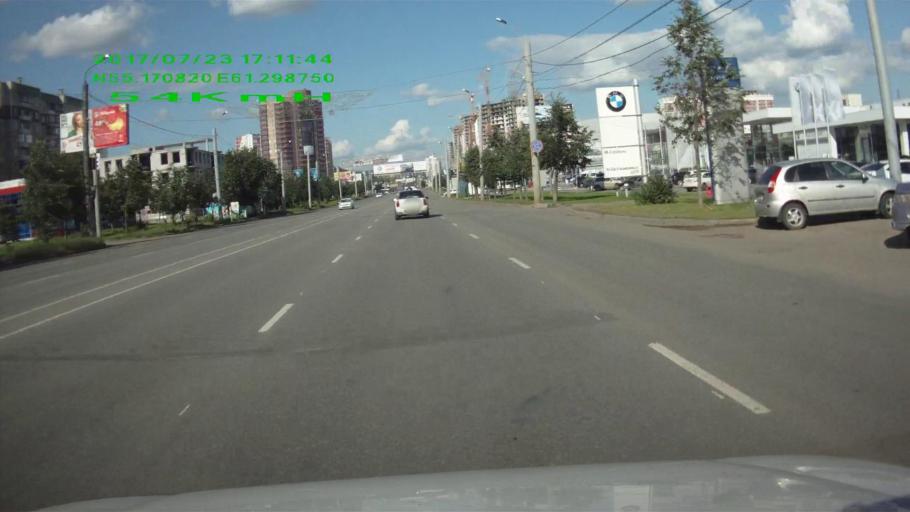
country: RU
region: Chelyabinsk
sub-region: Gorod Chelyabinsk
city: Chelyabinsk
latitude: 55.1710
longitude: 61.2992
